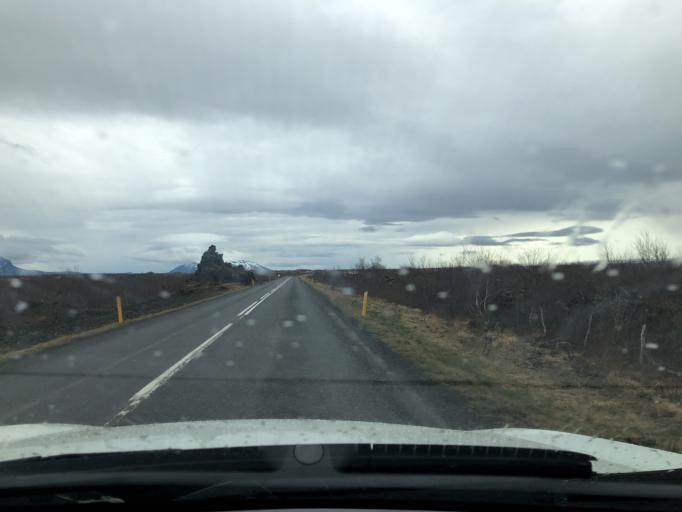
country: IS
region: Northeast
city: Laugar
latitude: 65.6054
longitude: -16.9224
